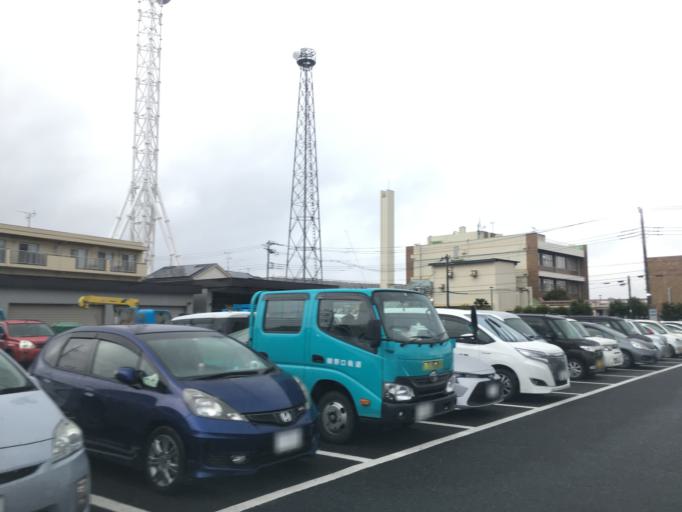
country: JP
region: Saitama
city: Koshigaya
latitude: 35.8919
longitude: 139.7897
